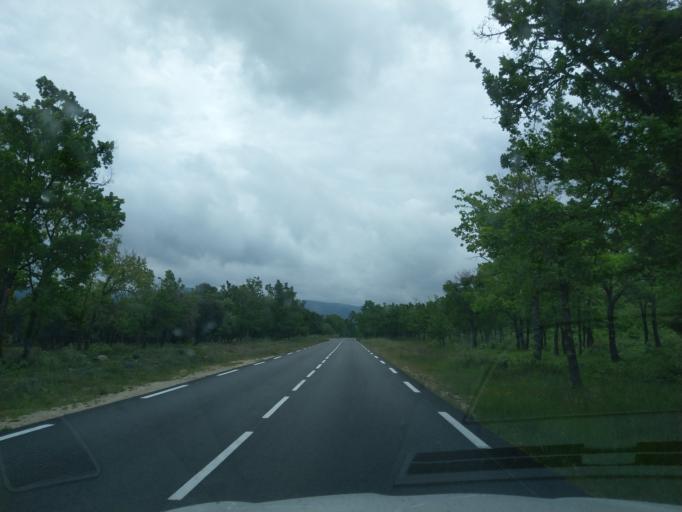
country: FR
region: Provence-Alpes-Cote d'Azur
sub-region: Departement du Var
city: Signes
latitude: 43.2772
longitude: 5.8120
